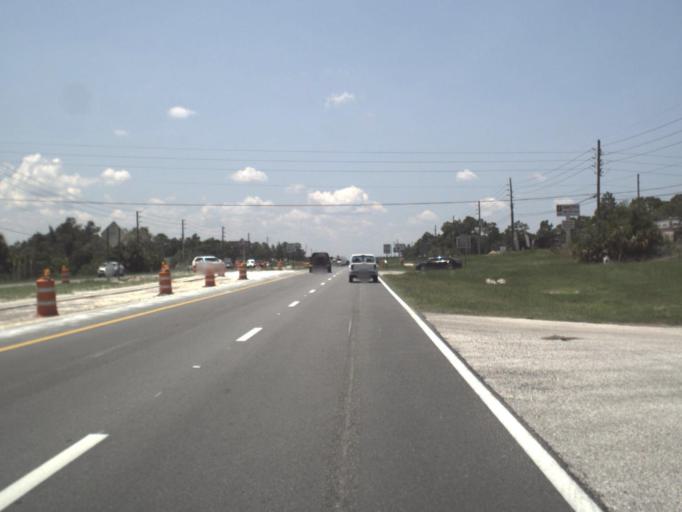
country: US
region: Florida
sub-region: Hernando County
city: North Weeki Wachee
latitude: 28.5489
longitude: -82.5637
